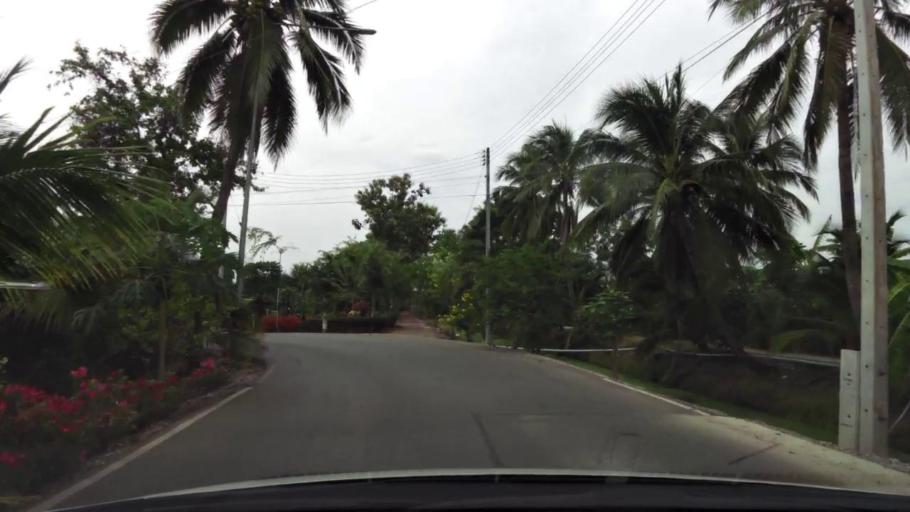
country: TH
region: Ratchaburi
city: Damnoen Saduak
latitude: 13.5748
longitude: 99.9883
